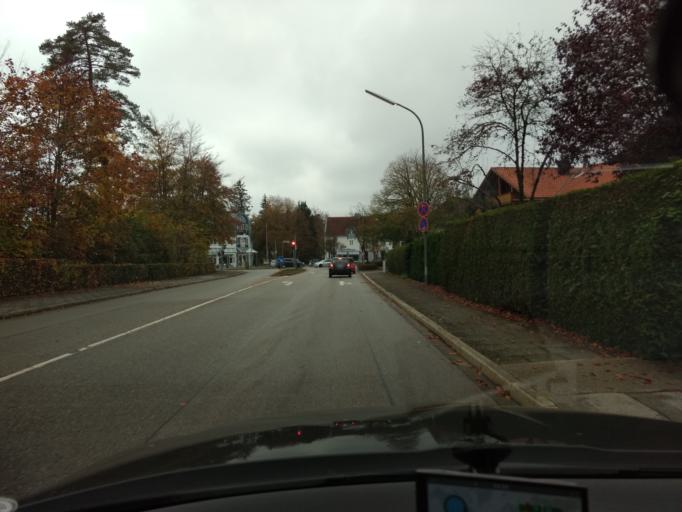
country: DE
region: Bavaria
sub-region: Upper Bavaria
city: Geretsried
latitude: 47.8704
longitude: 11.4736
